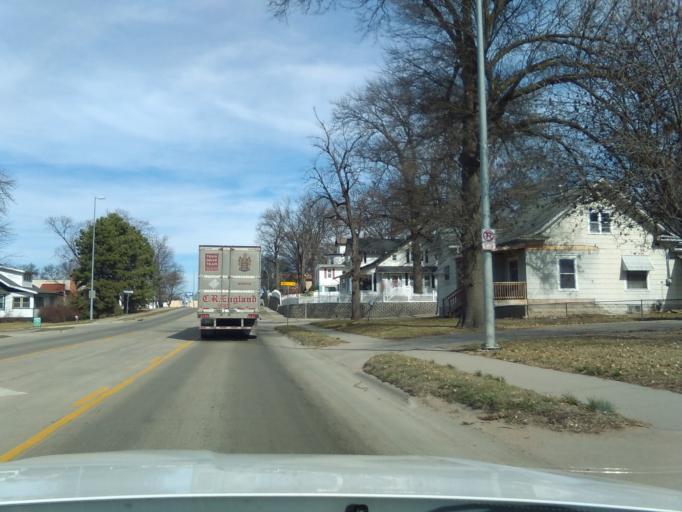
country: US
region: Nebraska
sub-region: Saline County
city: Crete
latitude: 40.6265
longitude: -96.9555
